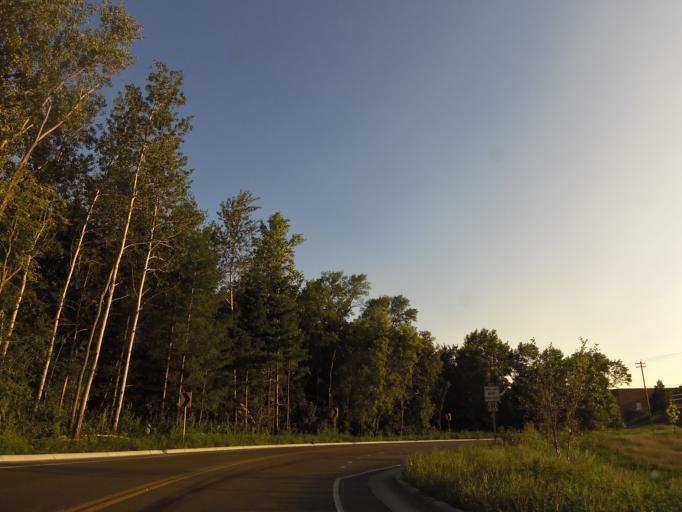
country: US
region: Minnesota
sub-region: Washington County
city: Oak Park Heights
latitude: 45.0347
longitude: -92.8065
